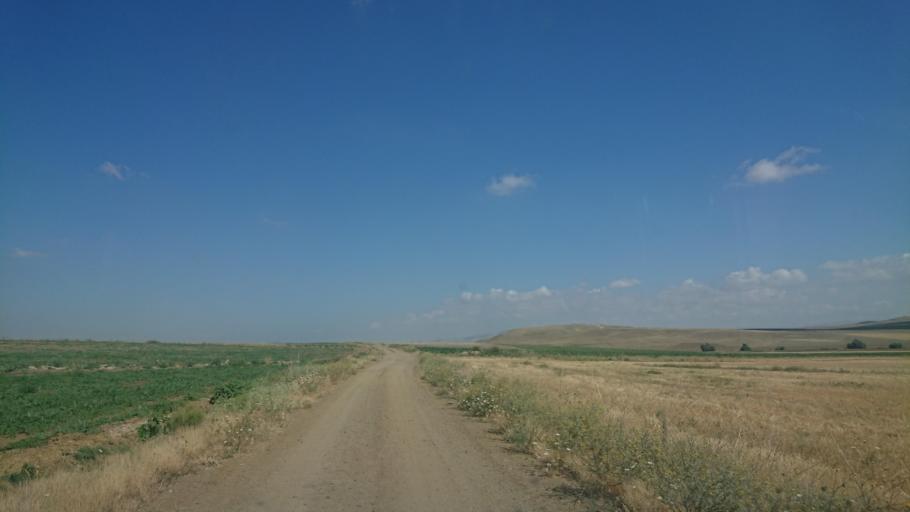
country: TR
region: Aksaray
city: Sariyahsi
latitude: 38.9650
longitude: 33.9251
